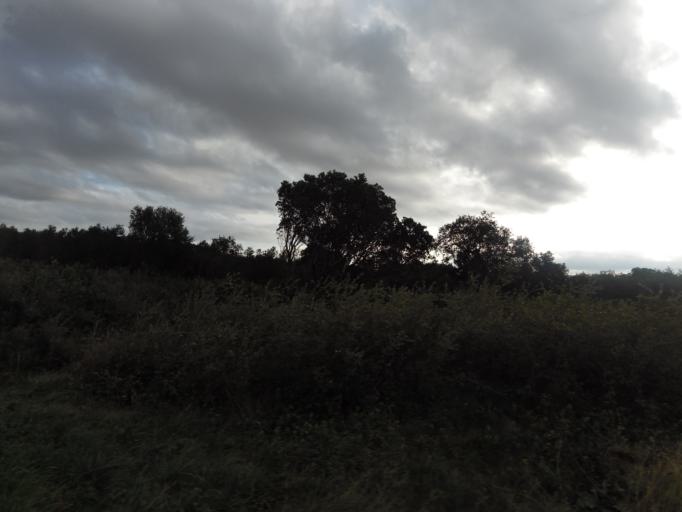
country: FR
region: Languedoc-Roussillon
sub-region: Departement du Gard
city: Clarensac
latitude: 43.8360
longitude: 4.1896
